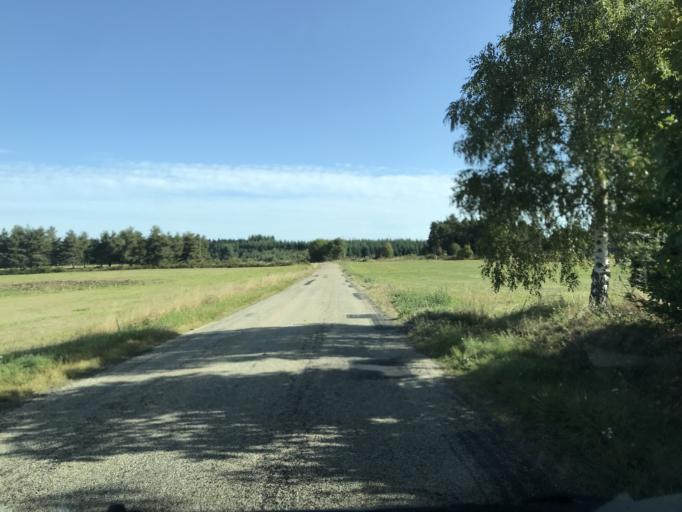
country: FR
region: Rhone-Alpes
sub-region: Departement de l'Ardeche
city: Saint-Agreve
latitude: 45.0253
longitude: 4.4230
